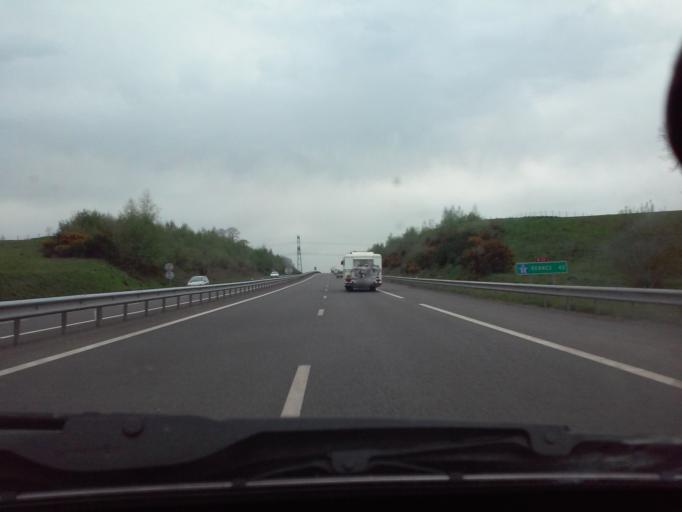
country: FR
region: Brittany
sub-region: Departement d'Ille-et-Vilaine
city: Lecousse
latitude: 48.3528
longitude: -1.2406
